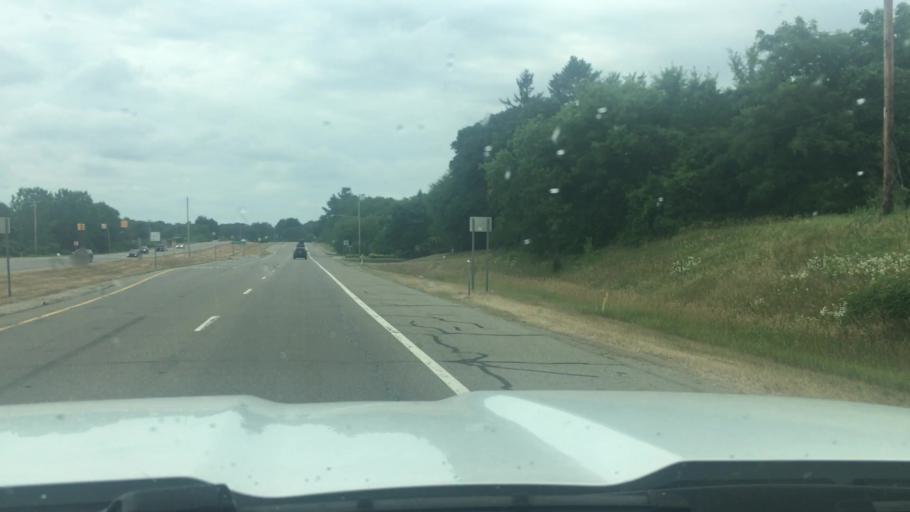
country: US
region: Michigan
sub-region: Kent County
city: Forest Hills
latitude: 42.9631
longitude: -85.5384
